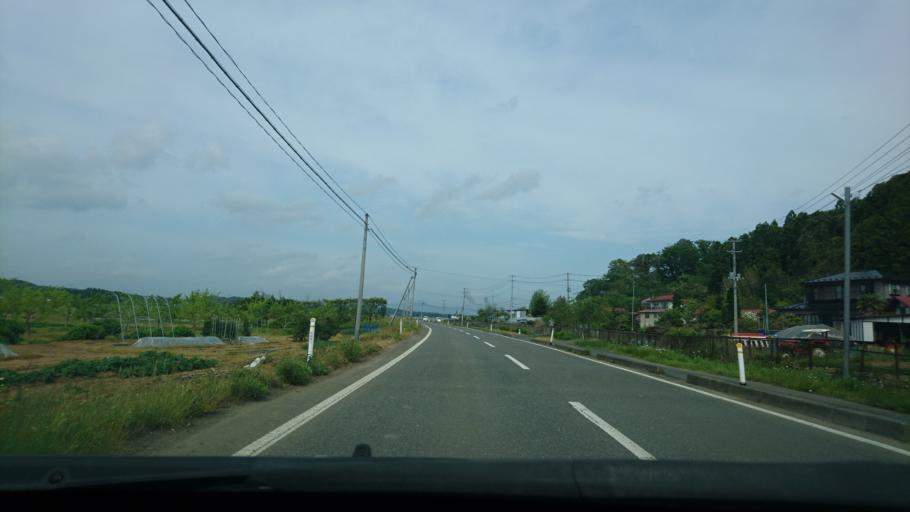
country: JP
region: Iwate
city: Ichinoseki
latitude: 38.8129
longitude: 141.0597
